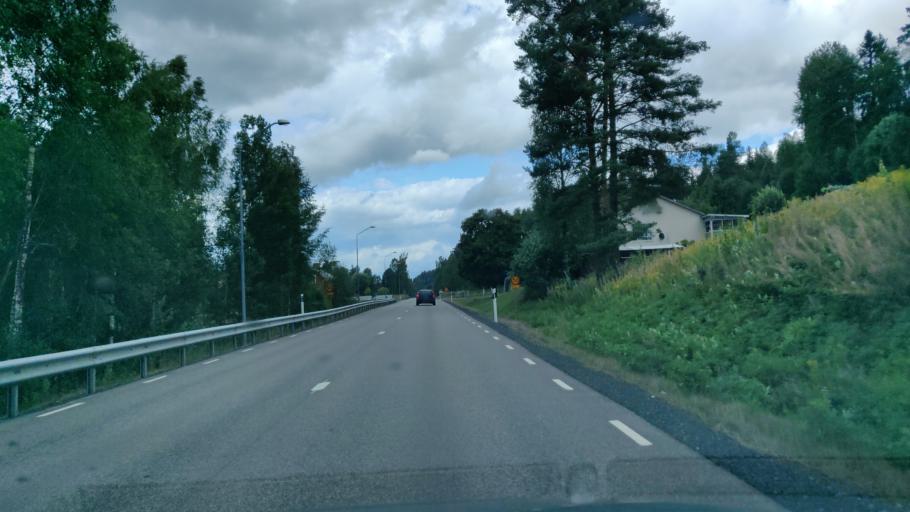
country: SE
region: Vaermland
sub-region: Torsby Kommun
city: Torsby
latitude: 60.6059
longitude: 13.0573
